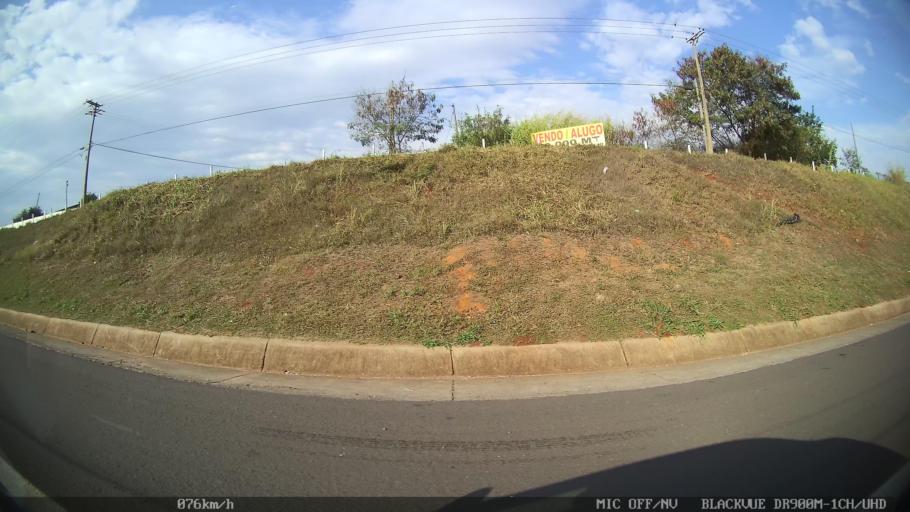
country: BR
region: Sao Paulo
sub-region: Paulinia
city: Paulinia
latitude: -22.7818
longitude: -47.1337
